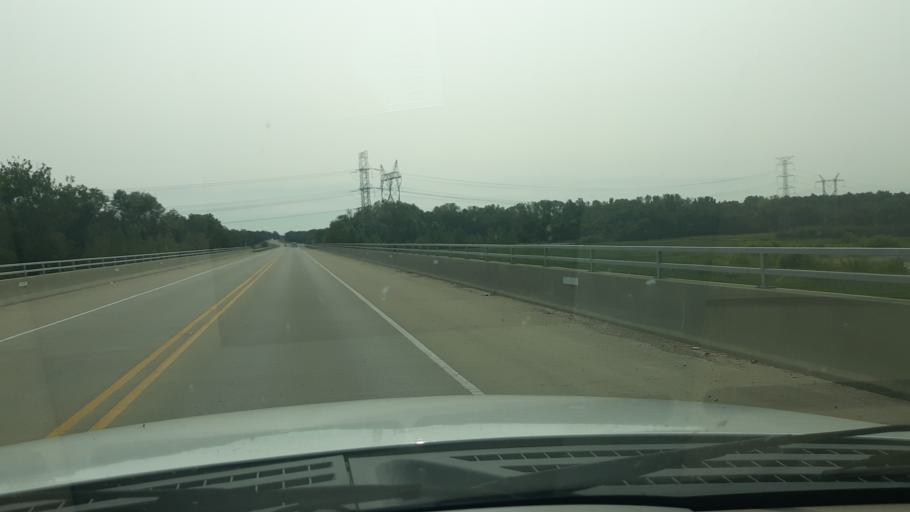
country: US
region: Illinois
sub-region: Wabash County
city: Mount Carmel
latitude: 38.3961
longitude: -87.7517
